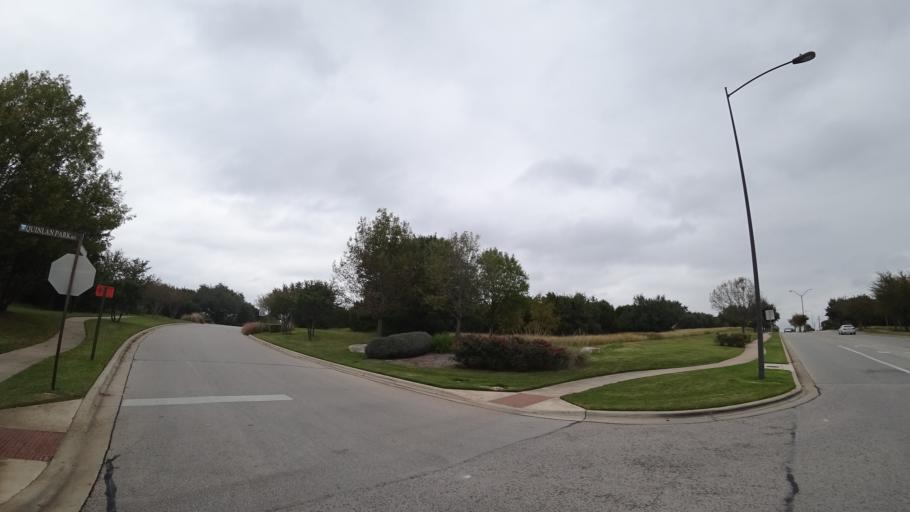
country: US
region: Texas
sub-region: Travis County
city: Bee Cave
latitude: 30.3561
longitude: -97.9088
